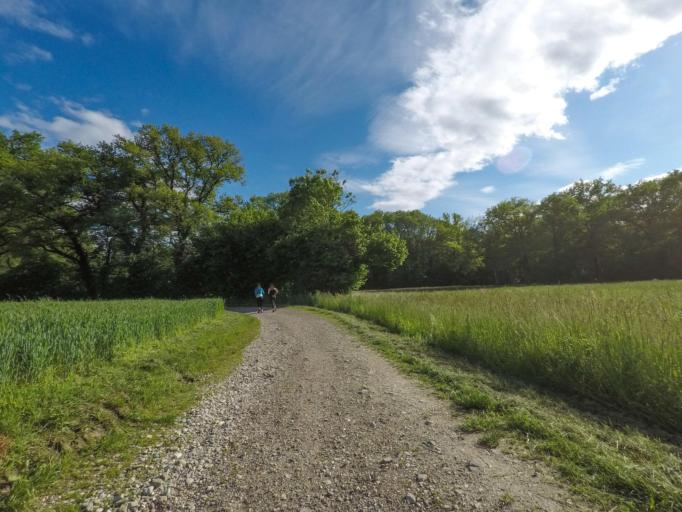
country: FR
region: Rhone-Alpes
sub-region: Departement de l'Ain
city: Chevry
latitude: 46.2694
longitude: 6.0627
